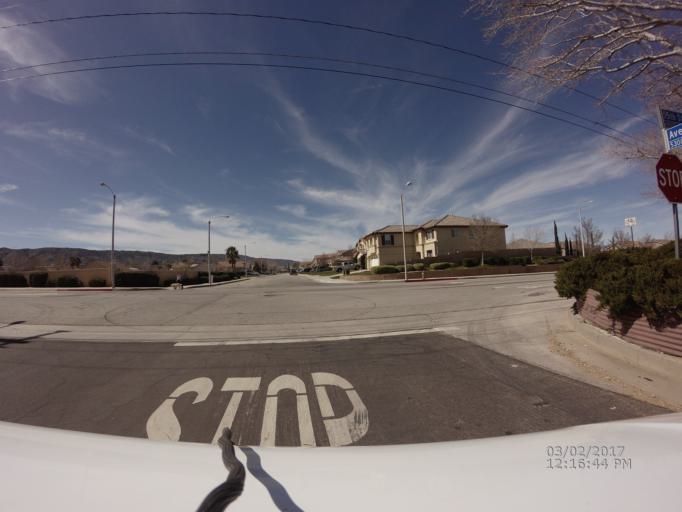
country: US
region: California
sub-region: Los Angeles County
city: Quartz Hill
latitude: 34.6474
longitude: -118.2272
